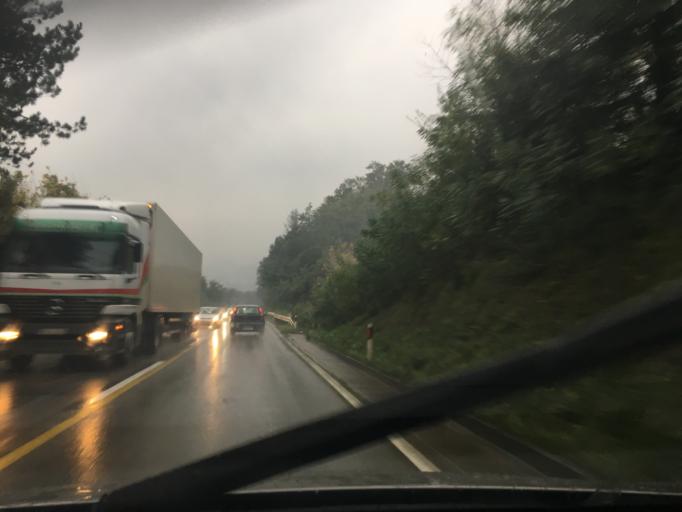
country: RS
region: Central Serbia
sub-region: Pcinjski Okrug
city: Vladicin Han
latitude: 42.8206
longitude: 22.1246
